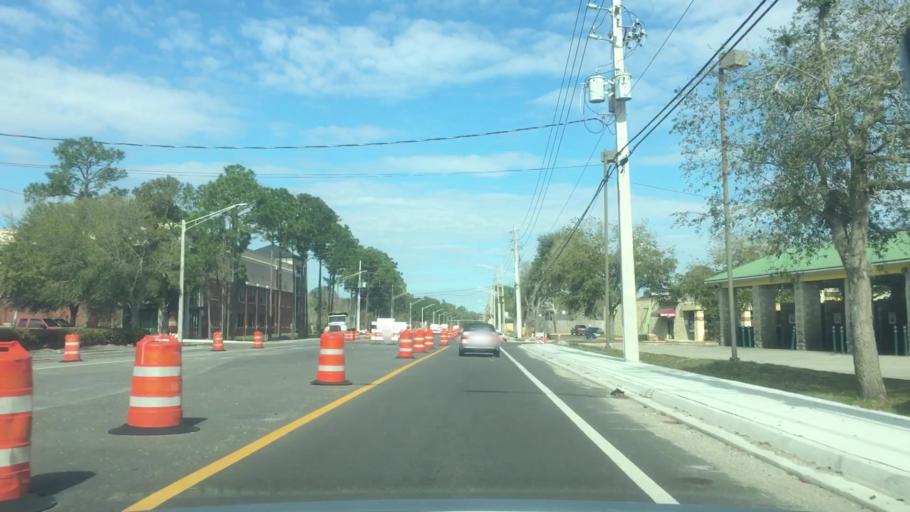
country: US
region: Florida
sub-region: Duval County
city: Atlantic Beach
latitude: 30.3195
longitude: -81.4728
